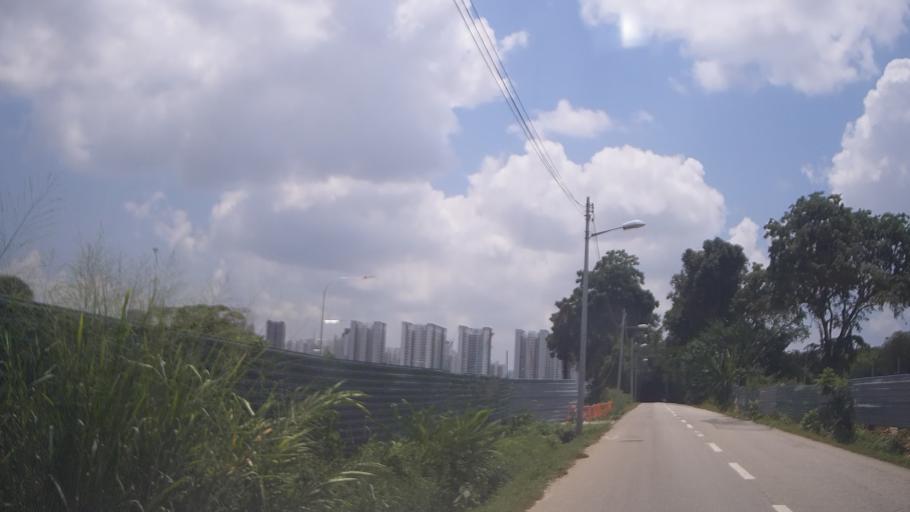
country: MY
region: Johor
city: Kampung Pasir Gudang Baru
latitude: 1.3957
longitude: 103.8657
